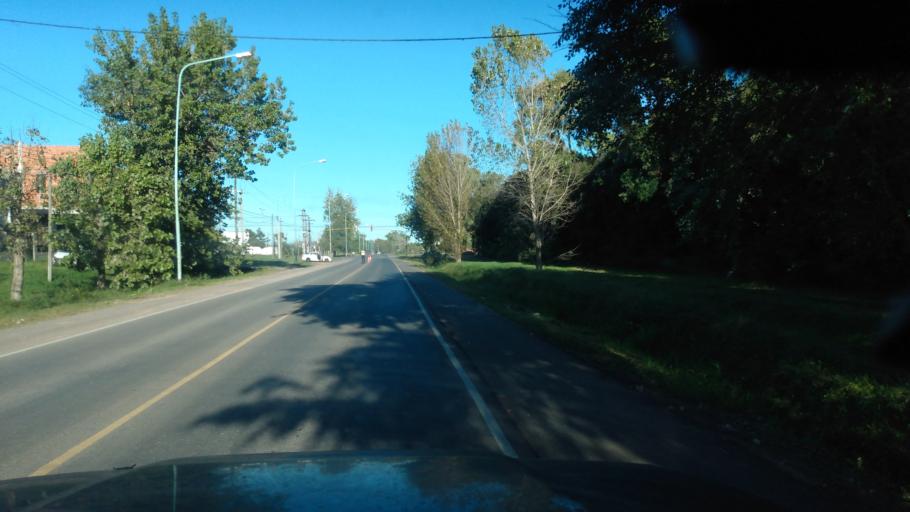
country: AR
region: Buenos Aires
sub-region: Partido de Lujan
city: Lujan
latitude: -34.5615
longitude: -59.1364
